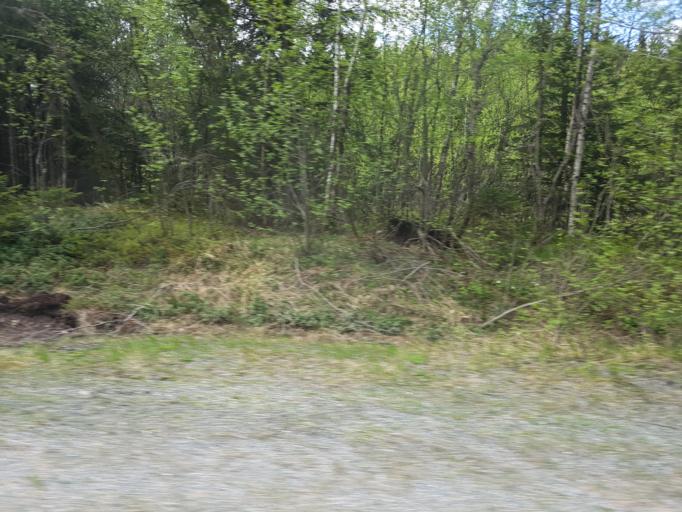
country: NO
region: Nord-Trondelag
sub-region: Levanger
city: Skogn
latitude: 63.6523
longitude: 11.2401
